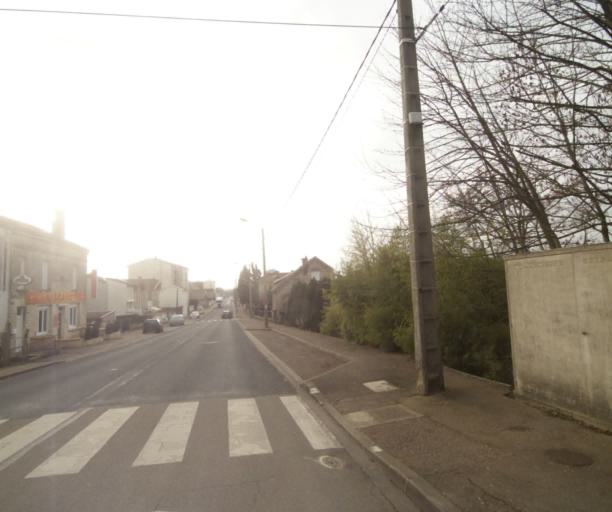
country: FR
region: Champagne-Ardenne
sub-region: Departement de la Haute-Marne
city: Saint-Dizier
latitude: 48.6420
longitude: 4.9332
